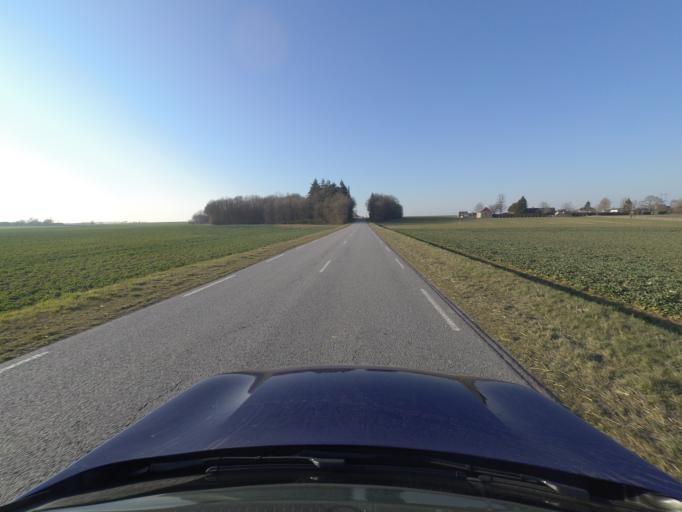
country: FR
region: Haute-Normandie
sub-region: Departement de l'Eure
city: Damville
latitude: 48.8929
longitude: 1.0418
